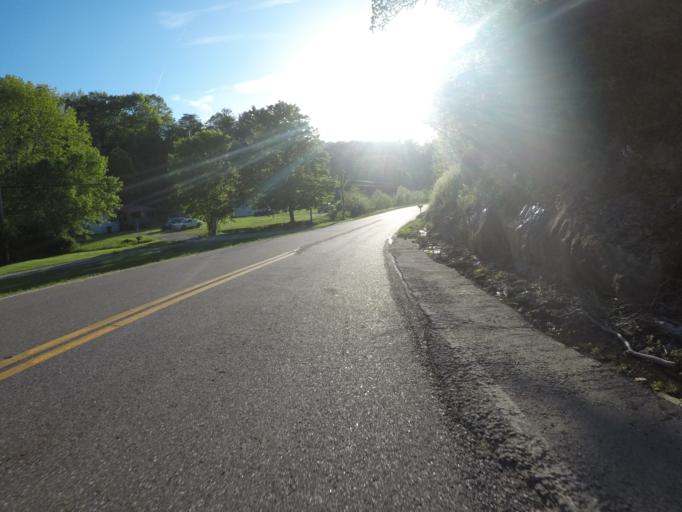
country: US
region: West Virginia
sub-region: Cabell County
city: Huntington
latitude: 38.5512
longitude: -82.4400
